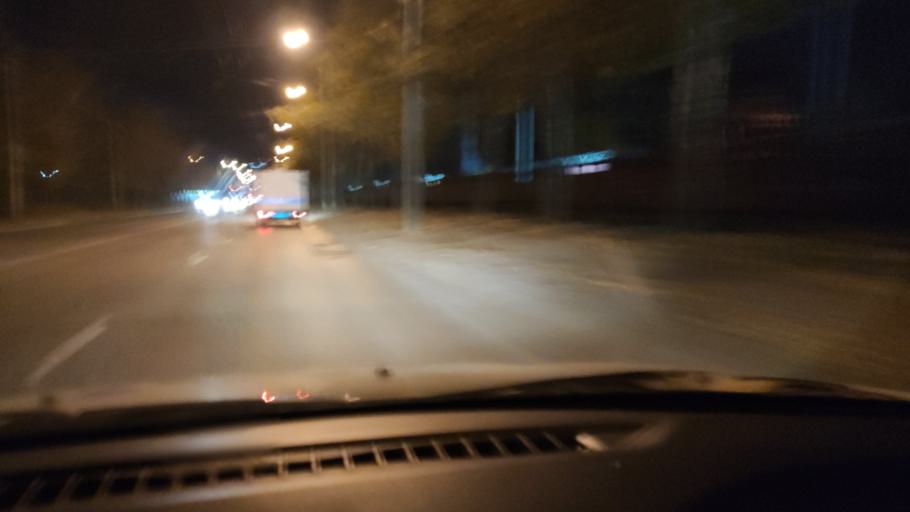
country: RU
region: Perm
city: Perm
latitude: 57.9789
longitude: 56.2467
